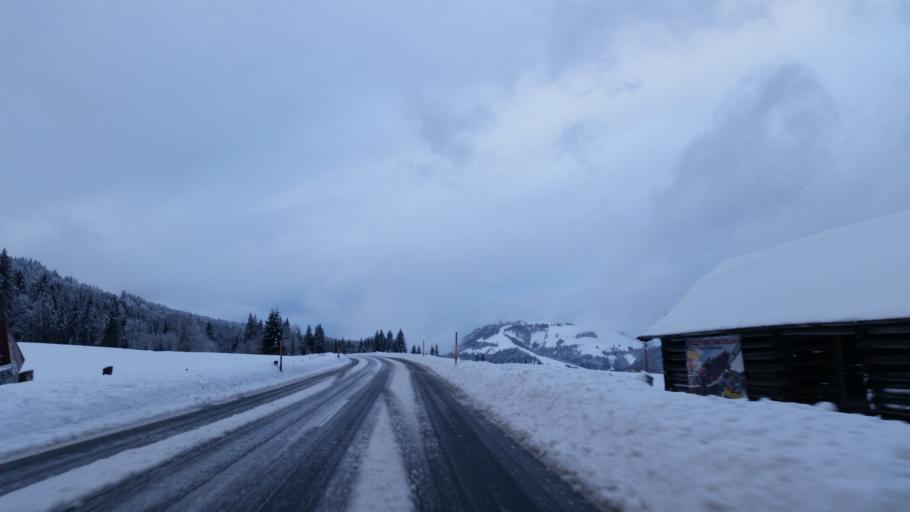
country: AT
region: Tyrol
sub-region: Politischer Bezirk Kitzbuhel
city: Hochfilzen
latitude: 47.4541
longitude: 12.6551
